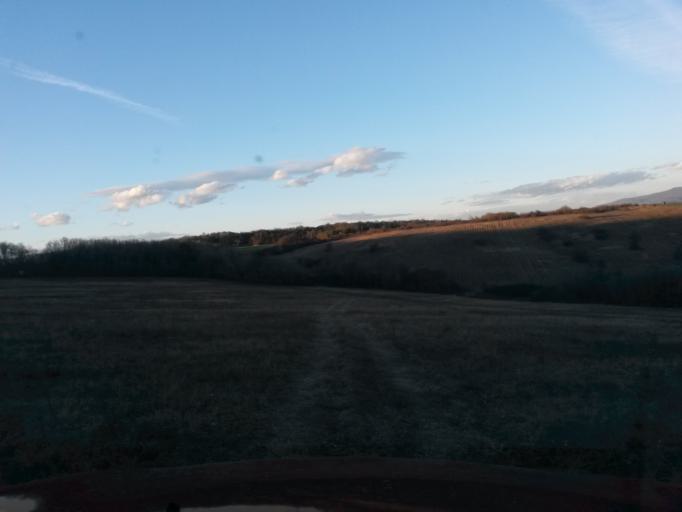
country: SK
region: Kosicky
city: Kosice
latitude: 48.7025
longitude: 21.3083
